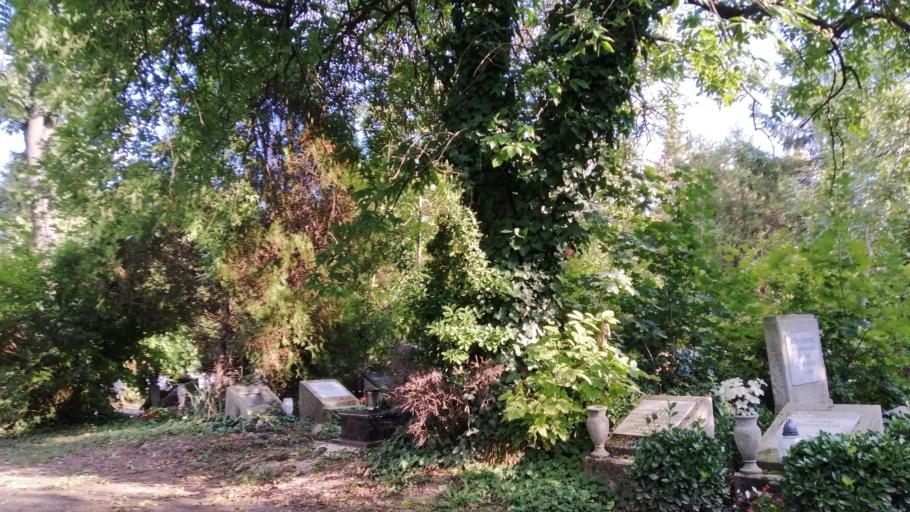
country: HU
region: Pest
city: Urom
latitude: 47.5691
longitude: 19.0243
